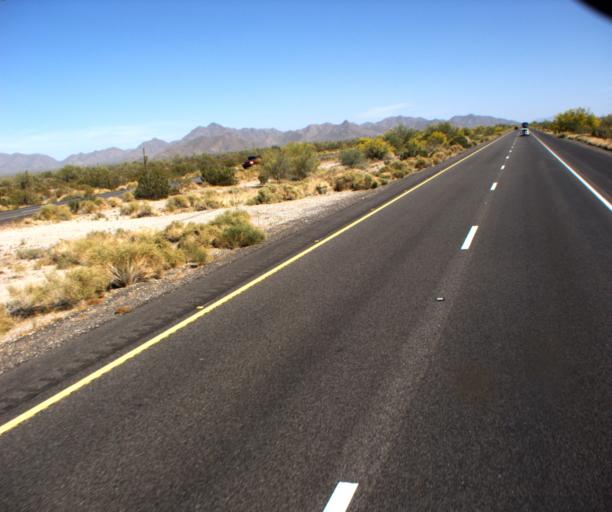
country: US
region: Arizona
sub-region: Maricopa County
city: Gila Bend
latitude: 32.8995
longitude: -112.5118
